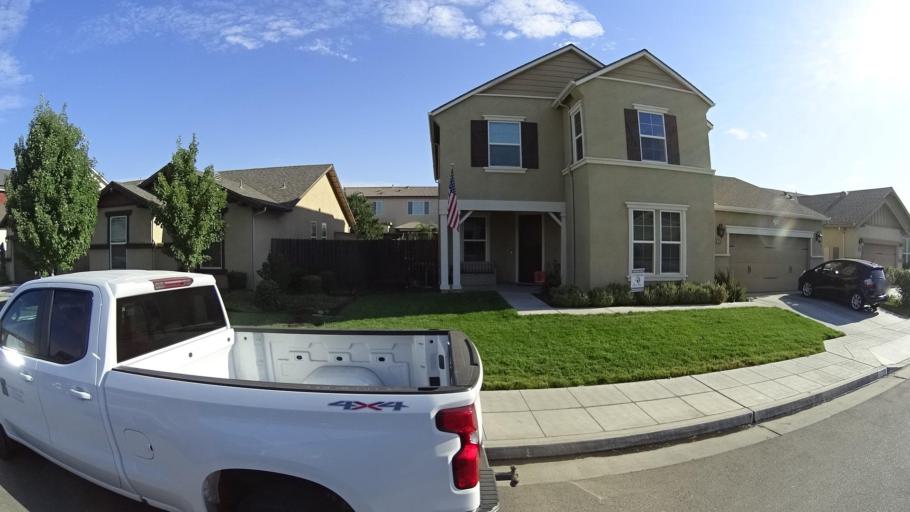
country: US
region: California
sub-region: Fresno County
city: Tarpey Village
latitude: 36.7893
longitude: -119.6692
